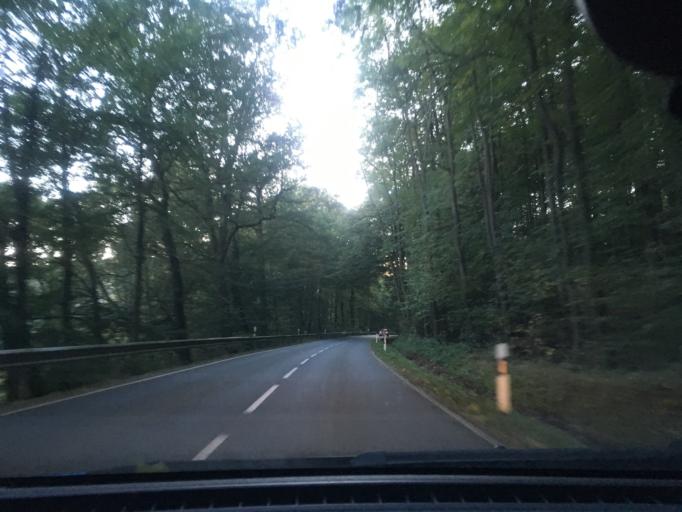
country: DE
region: Lower Saxony
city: Uslar
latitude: 51.6293
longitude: 9.6086
